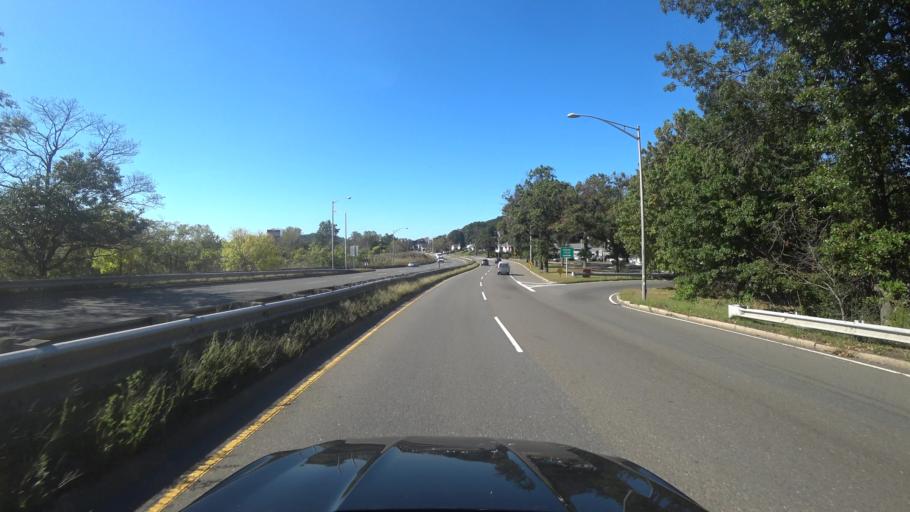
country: US
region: Massachusetts
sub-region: Suffolk County
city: Revere
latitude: 42.4043
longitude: -71.0182
